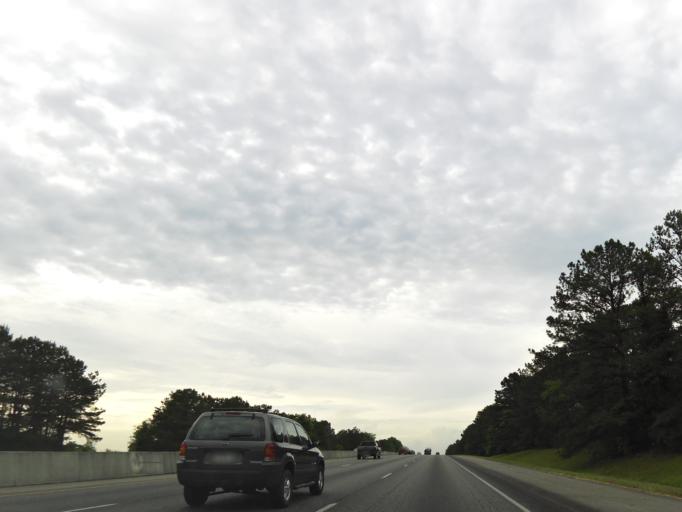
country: US
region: Georgia
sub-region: Bibb County
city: West Point
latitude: 32.9283
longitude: -83.8035
